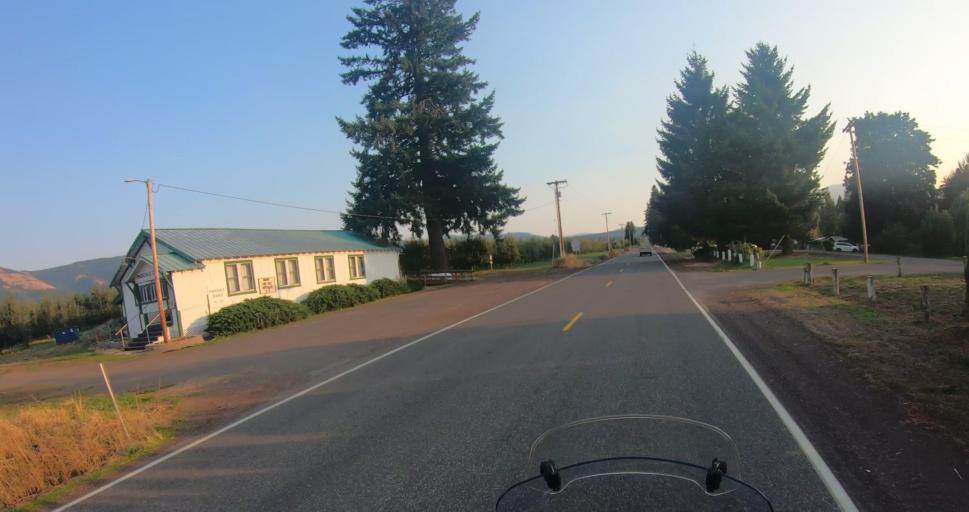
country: US
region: Oregon
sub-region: Hood River County
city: Odell
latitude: 45.5178
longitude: -121.5970
